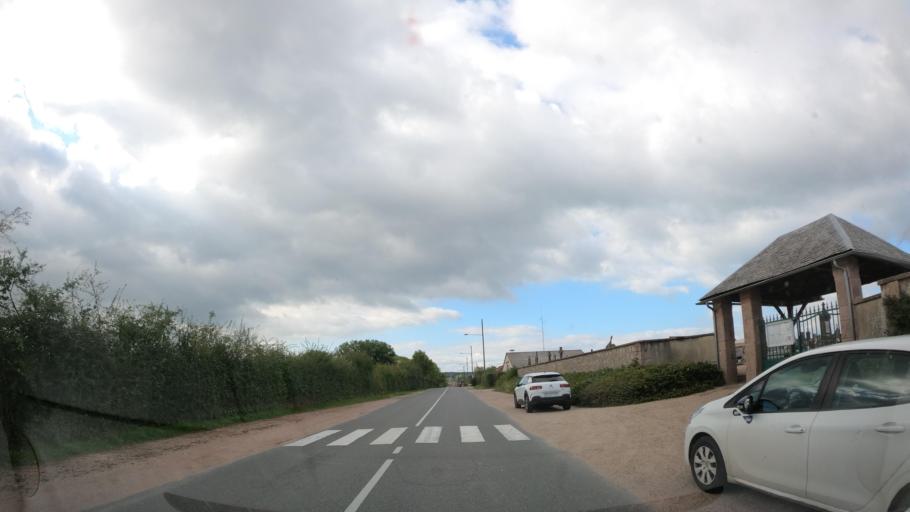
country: FR
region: Auvergne
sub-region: Departement de l'Allier
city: Lapalisse
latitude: 46.3777
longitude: 3.5976
